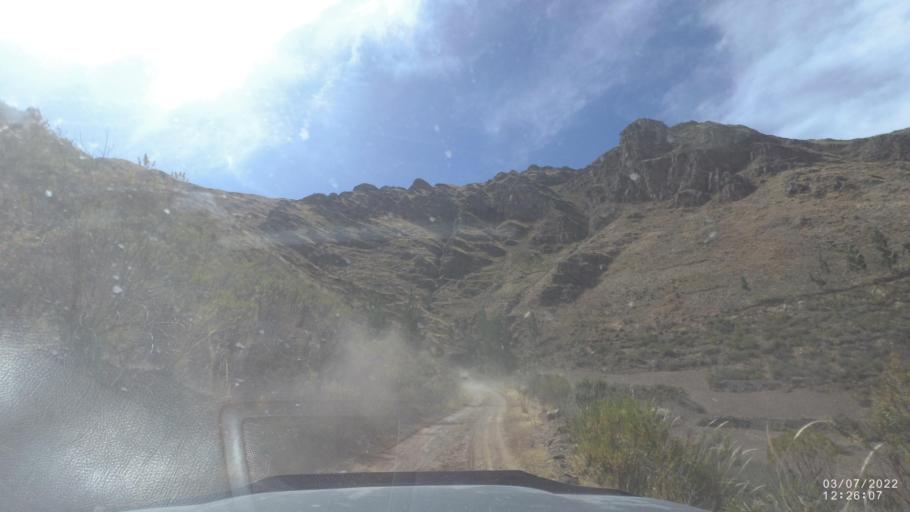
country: BO
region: Cochabamba
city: Irpa Irpa
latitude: -17.8089
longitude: -66.6172
